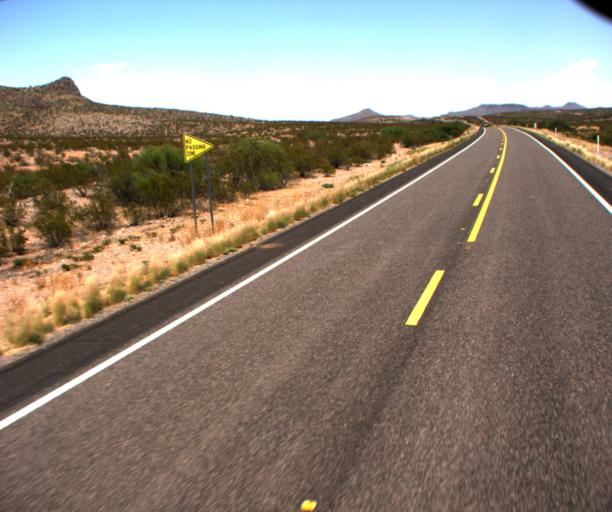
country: US
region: Arizona
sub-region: Greenlee County
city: Clifton
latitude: 32.7496
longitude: -109.3914
